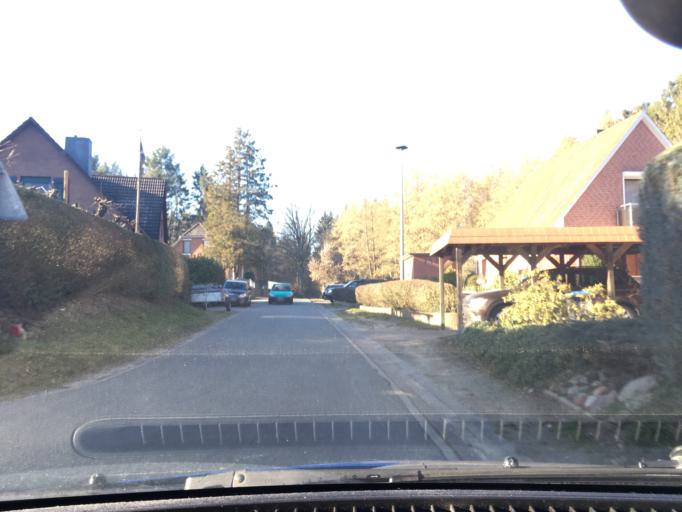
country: DE
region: Schleswig-Holstein
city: Schnakenbek
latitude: 53.3792
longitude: 10.5082
